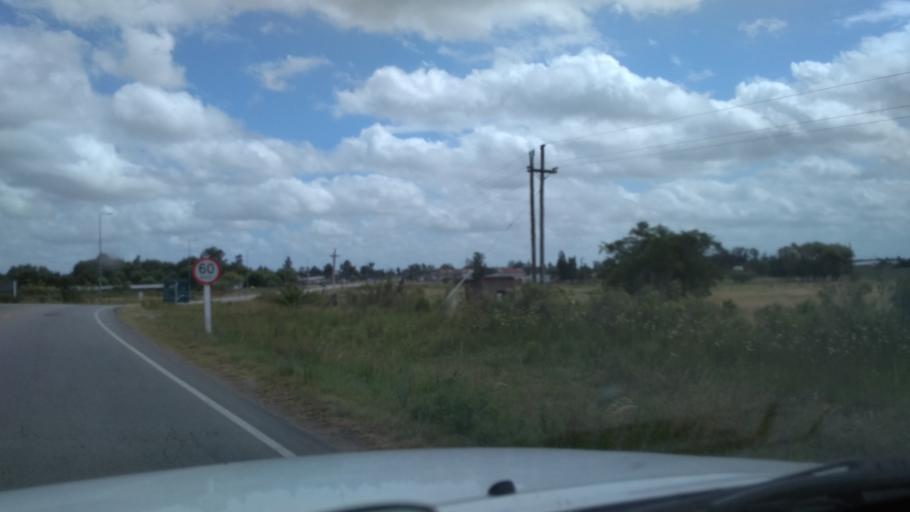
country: UY
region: Canelones
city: San Bautista
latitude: -34.4348
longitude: -55.9609
